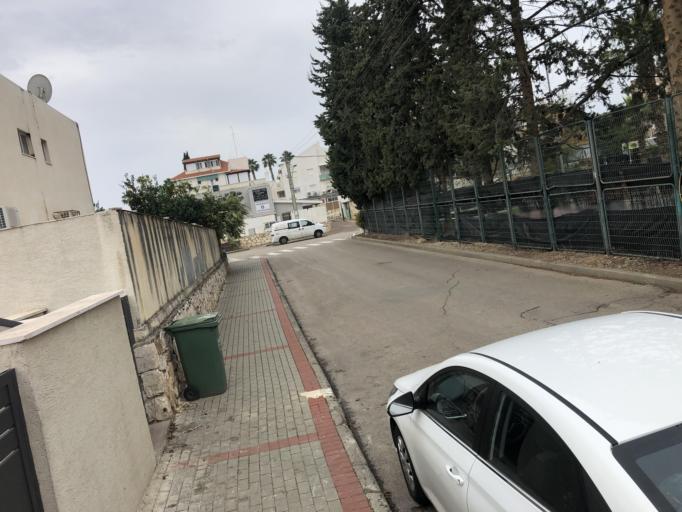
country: IL
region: Northern District
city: `Akko
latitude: 32.9293
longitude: 35.0940
